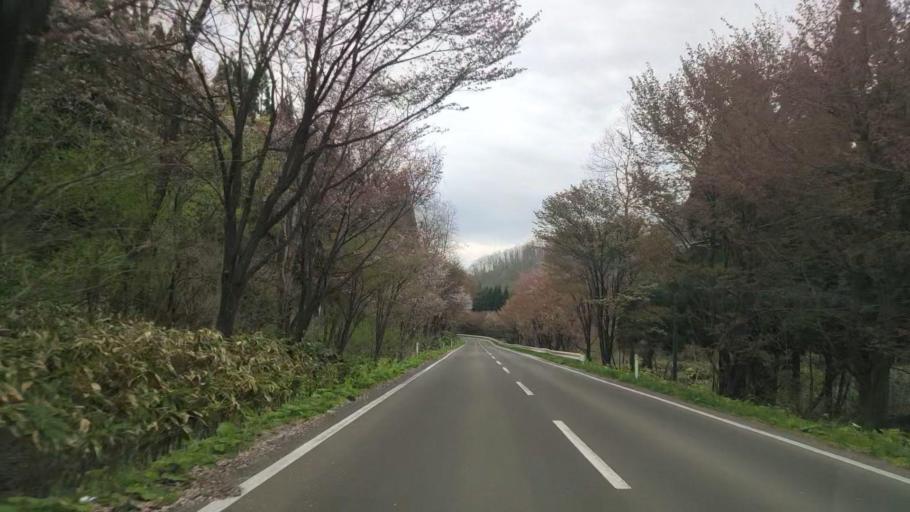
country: JP
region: Akita
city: Hanawa
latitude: 40.3513
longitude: 140.7764
